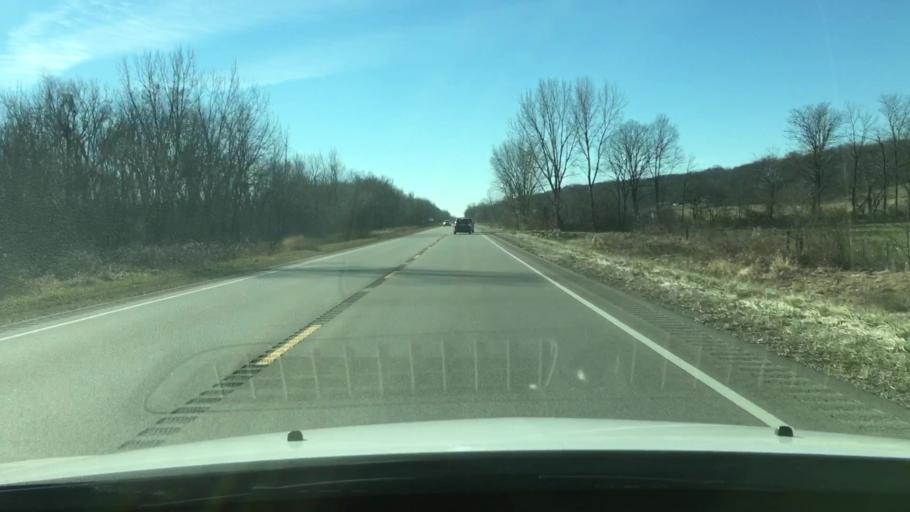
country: US
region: Illinois
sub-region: Peoria County
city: Glasford
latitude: 40.5445
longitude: -89.8595
